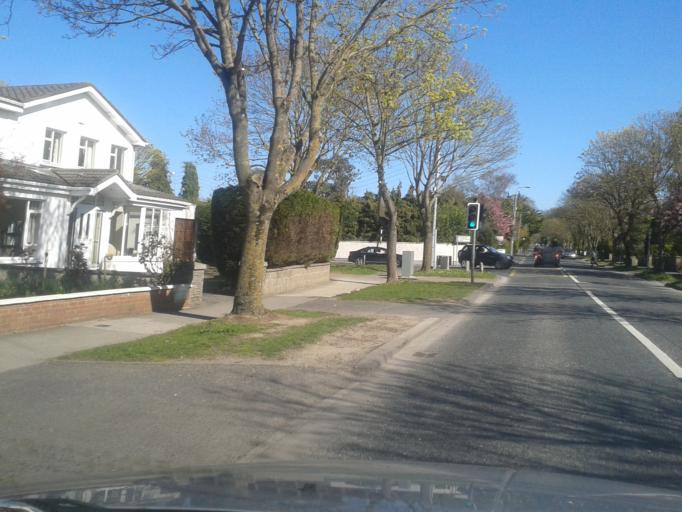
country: IE
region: Leinster
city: Malahide
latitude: 53.4477
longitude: -6.1781
